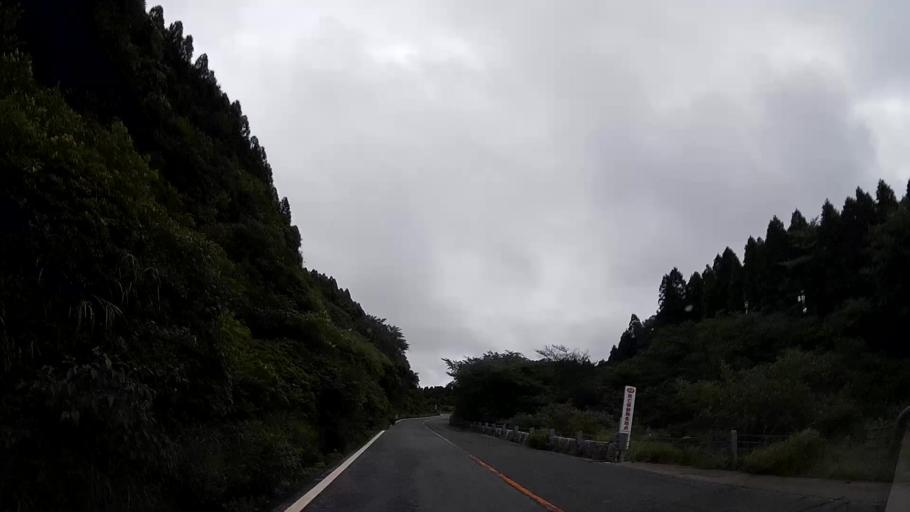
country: JP
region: Kumamoto
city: Aso
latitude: 32.8893
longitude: 131.0524
